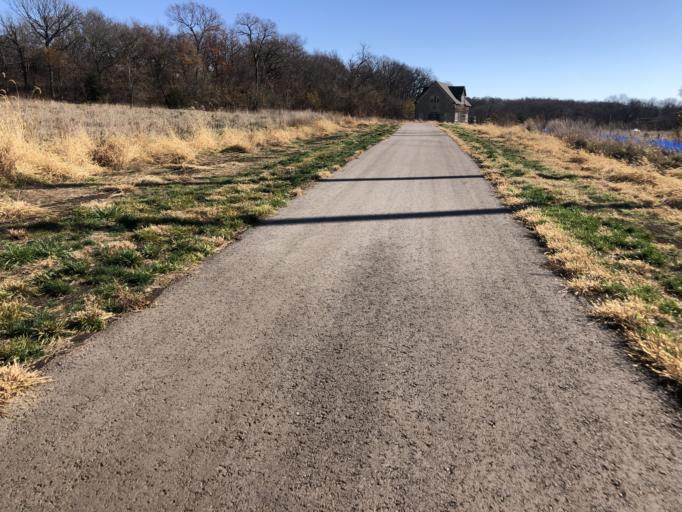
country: US
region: Kansas
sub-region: Johnson County
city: Gardner
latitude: 38.8721
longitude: -94.9507
